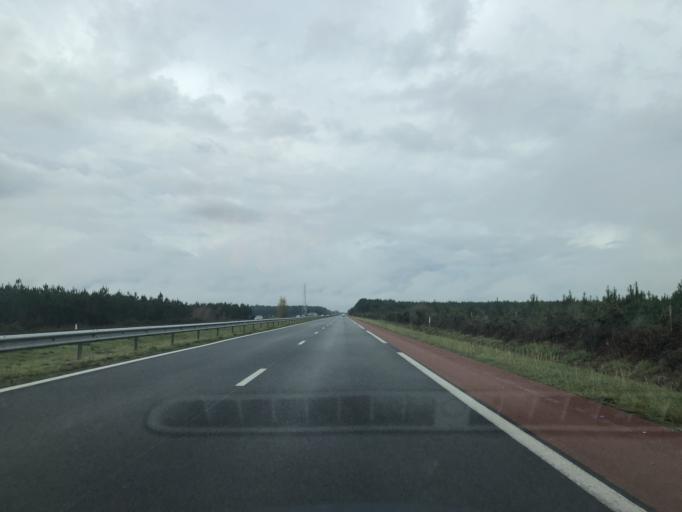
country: FR
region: Aquitaine
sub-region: Departement de la Gironde
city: Marcheprime
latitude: 44.7887
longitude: -0.9003
